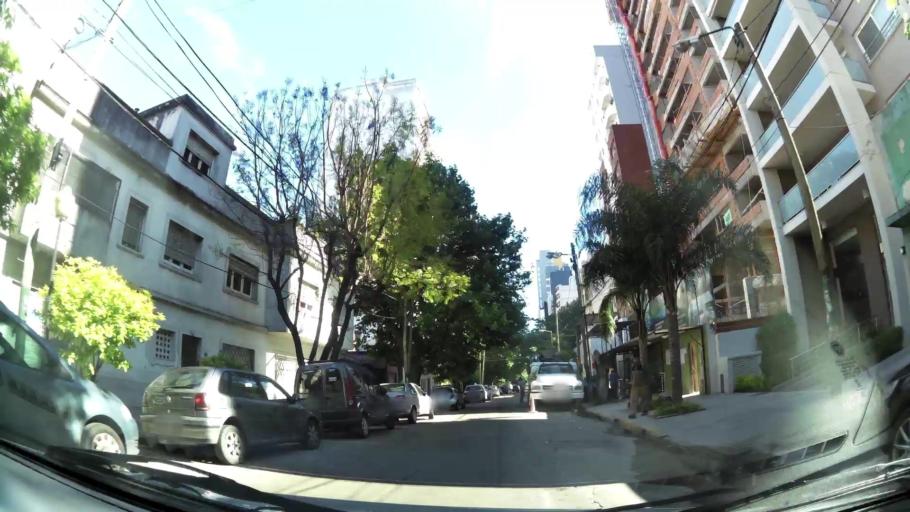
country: AR
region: Buenos Aires
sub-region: Partido de Lomas de Zamora
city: Lomas de Zamora
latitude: -34.7617
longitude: -58.4043
